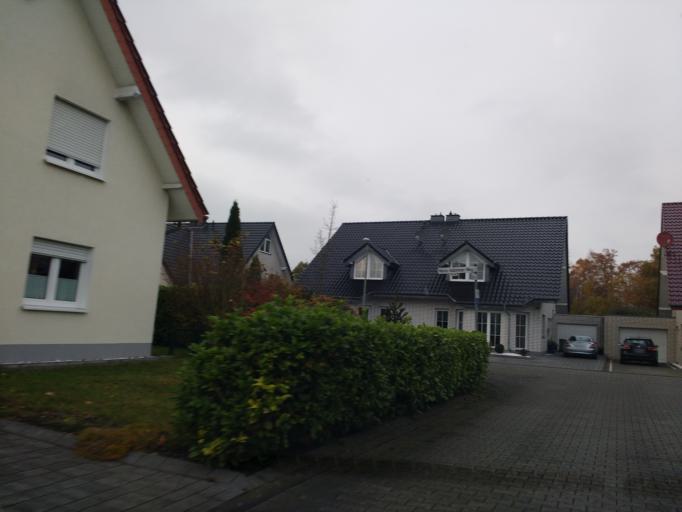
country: DE
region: North Rhine-Westphalia
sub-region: Regierungsbezirk Detmold
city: Hovelhof
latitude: 51.7653
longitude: 8.6571
